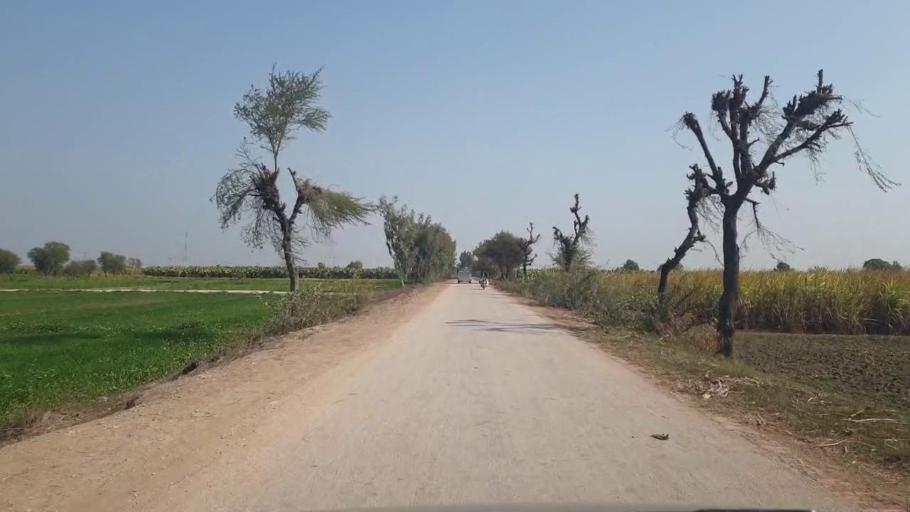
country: PK
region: Sindh
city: Tando Adam
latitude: 25.8202
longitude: 68.6456
